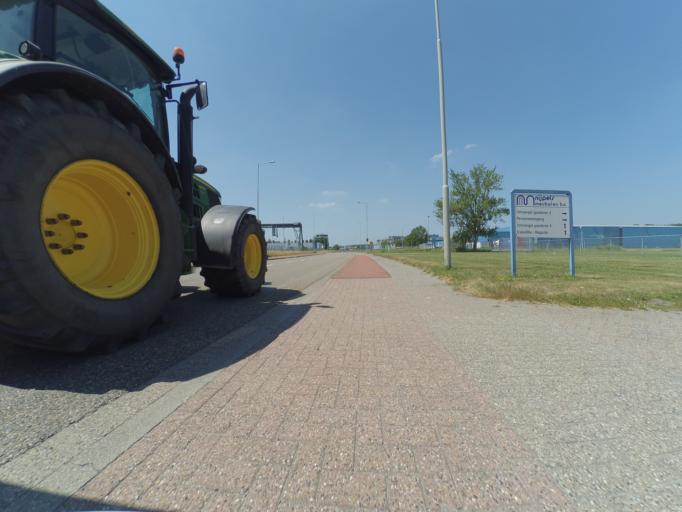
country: NL
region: North Brabant
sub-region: Gemeente Bergen op Zoom
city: Halsteren
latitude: 51.5070
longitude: 4.2684
